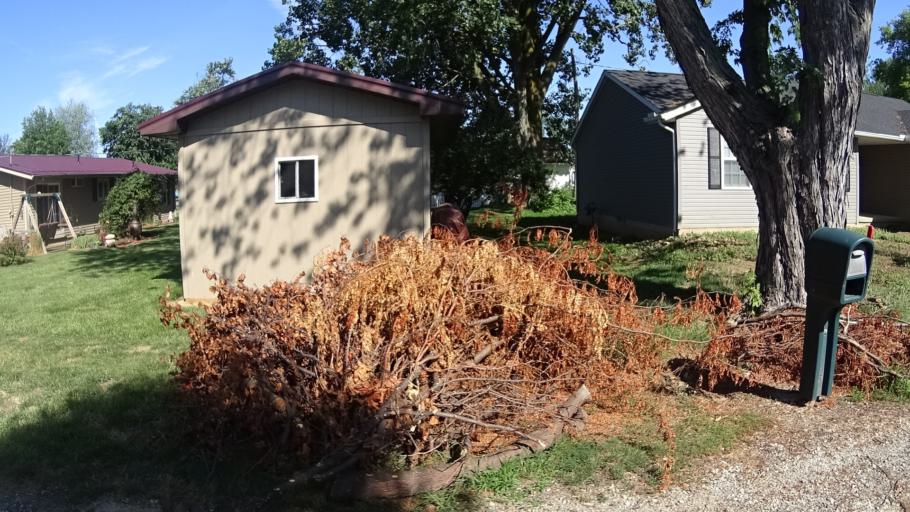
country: US
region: Ohio
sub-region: Ottawa County
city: Port Clinton
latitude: 41.4698
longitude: -82.8258
